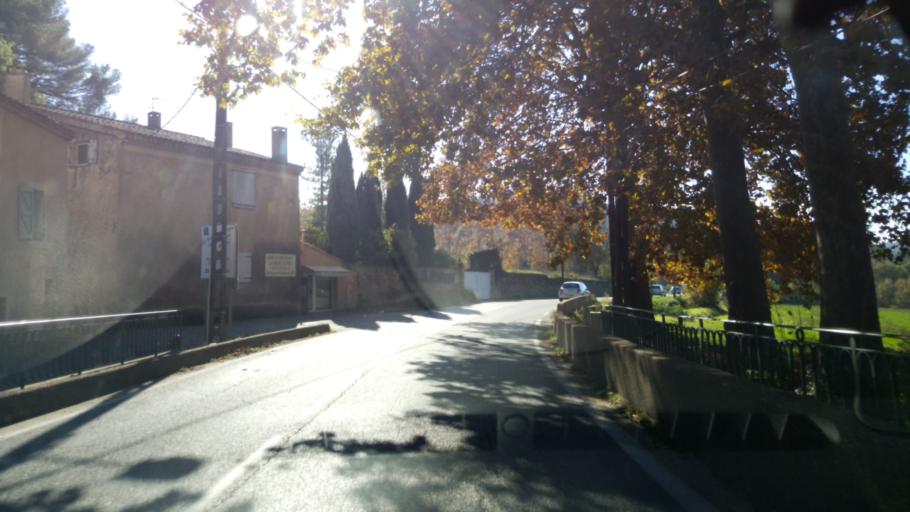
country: FR
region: Provence-Alpes-Cote d'Azur
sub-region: Departement du Var
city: Saint-Zacharie
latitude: 43.3800
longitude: 5.6994
